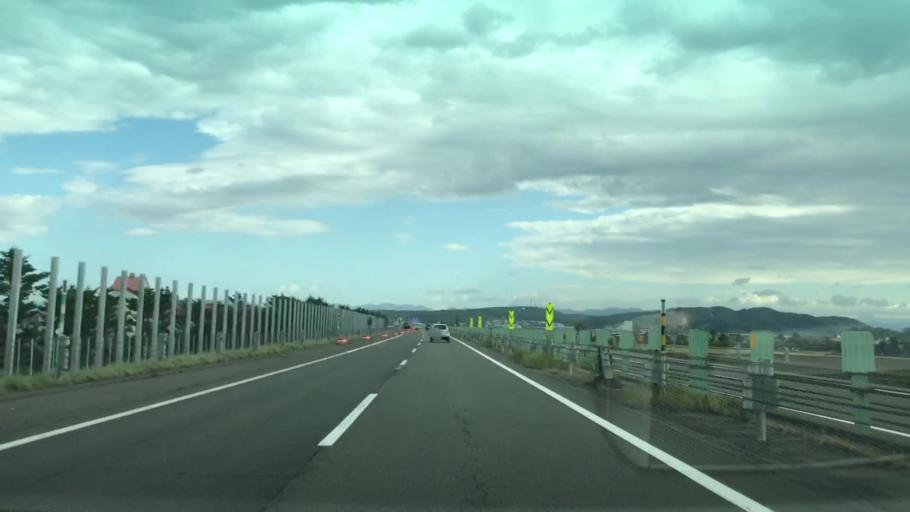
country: JP
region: Hokkaido
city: Iwamizawa
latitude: 43.1595
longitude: 141.7363
